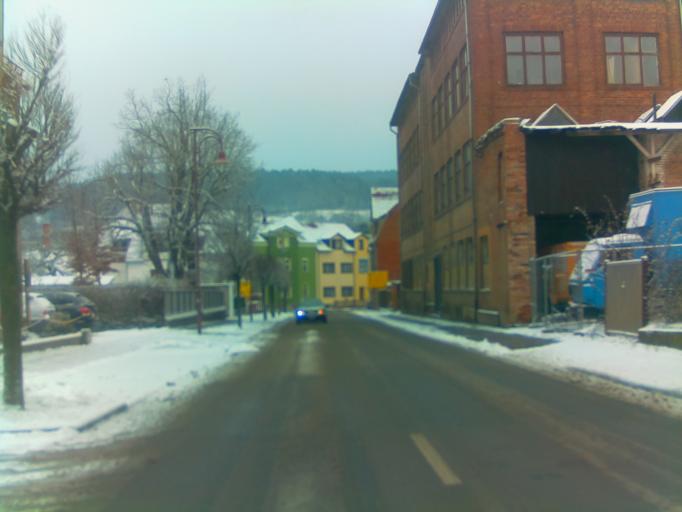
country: DE
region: Thuringia
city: Stadtilm
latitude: 50.7767
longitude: 11.0847
